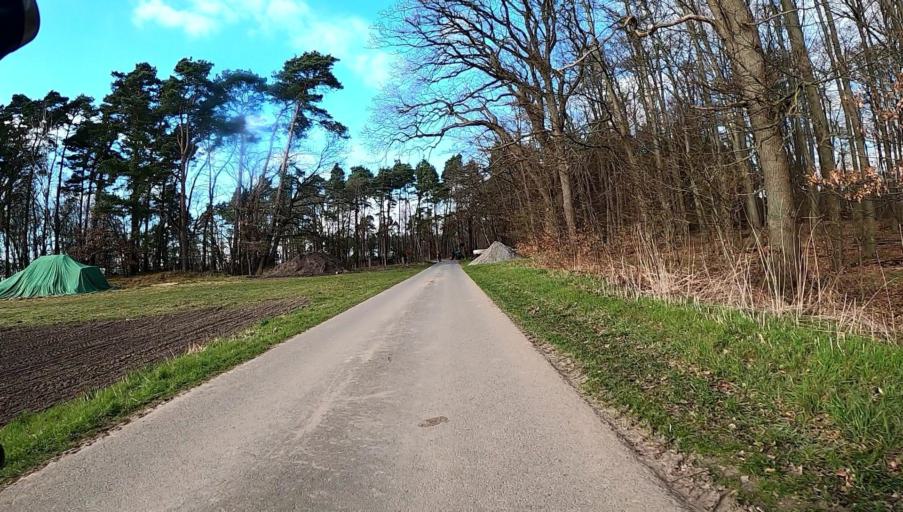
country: DE
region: Lower Saxony
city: Schwarmstedt
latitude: 52.6196
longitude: 9.6135
